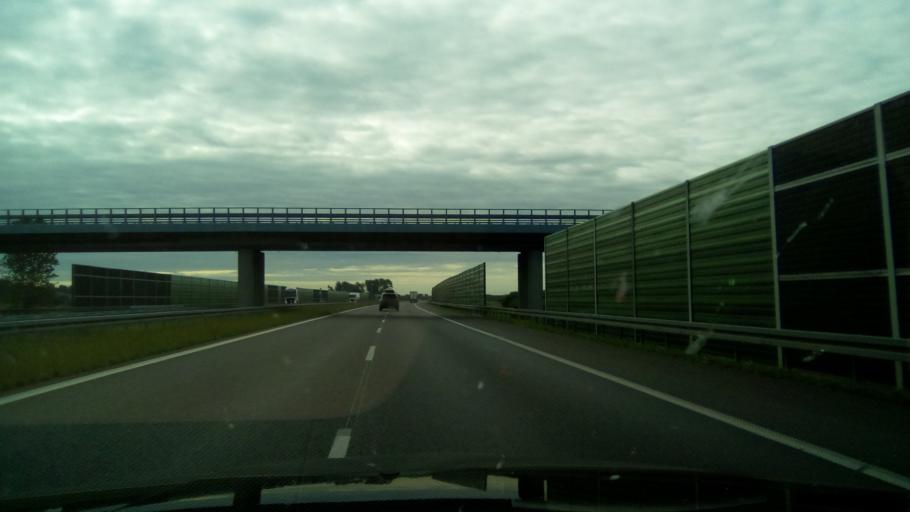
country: PL
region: Greater Poland Voivodeship
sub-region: Powiat kolski
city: Dabie
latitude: 52.1126
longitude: 18.7379
